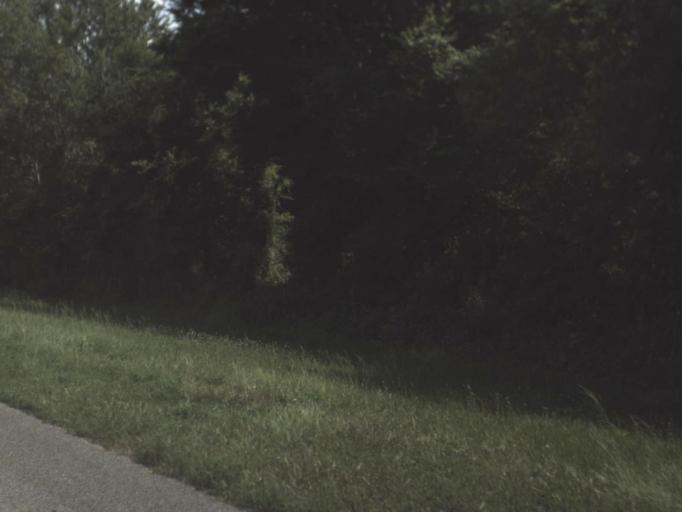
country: US
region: Florida
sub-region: Alachua County
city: Hawthorne
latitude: 29.6355
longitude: -82.1041
